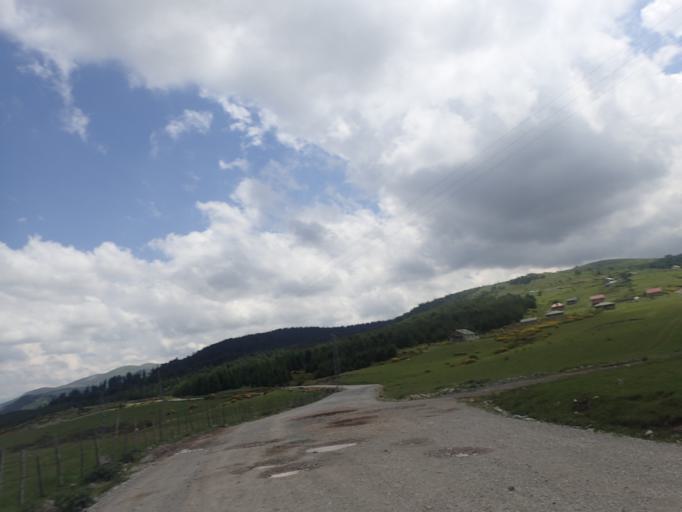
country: TR
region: Ordu
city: Topcam
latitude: 40.6839
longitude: 37.9332
